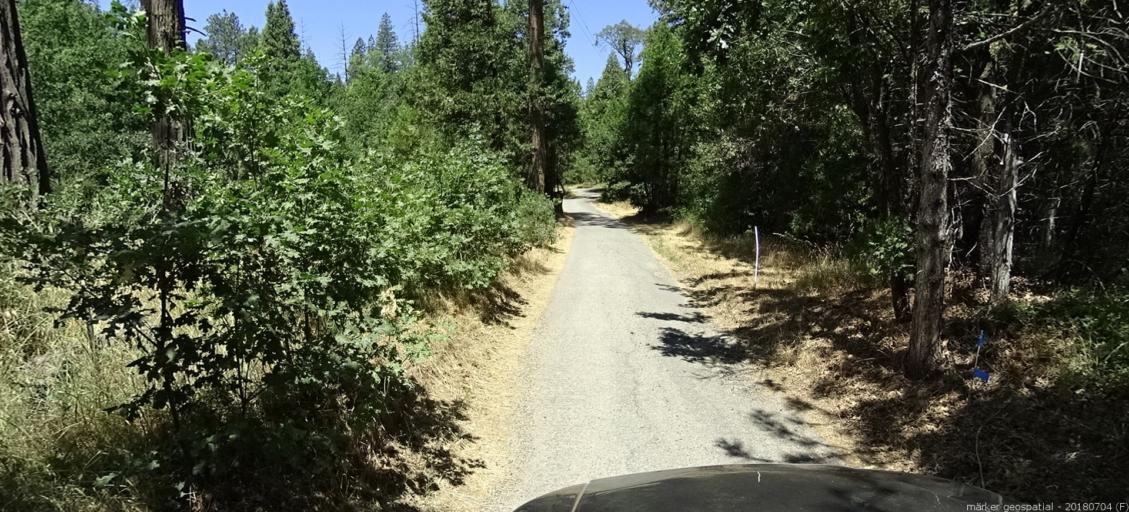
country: US
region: California
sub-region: Fresno County
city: Auberry
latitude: 37.2264
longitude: -119.4550
